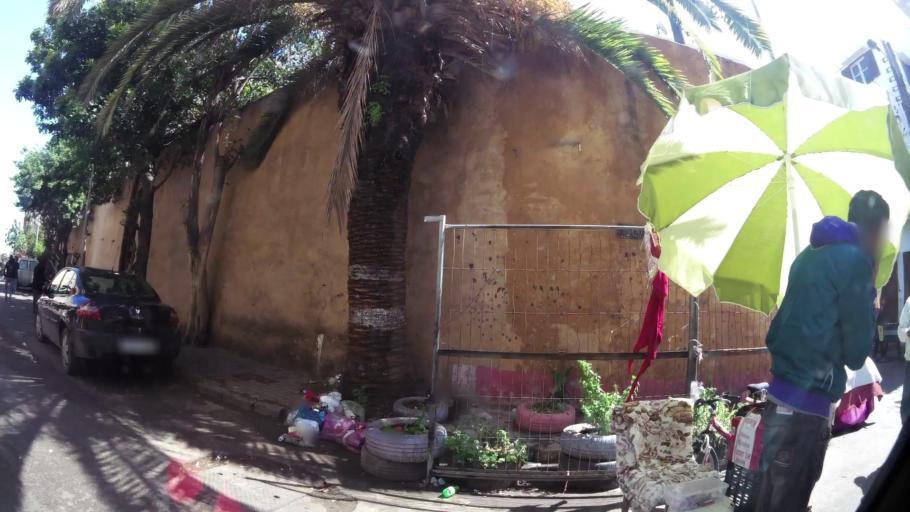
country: MA
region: Grand Casablanca
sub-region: Casablanca
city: Casablanca
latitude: 33.6000
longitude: -7.6231
